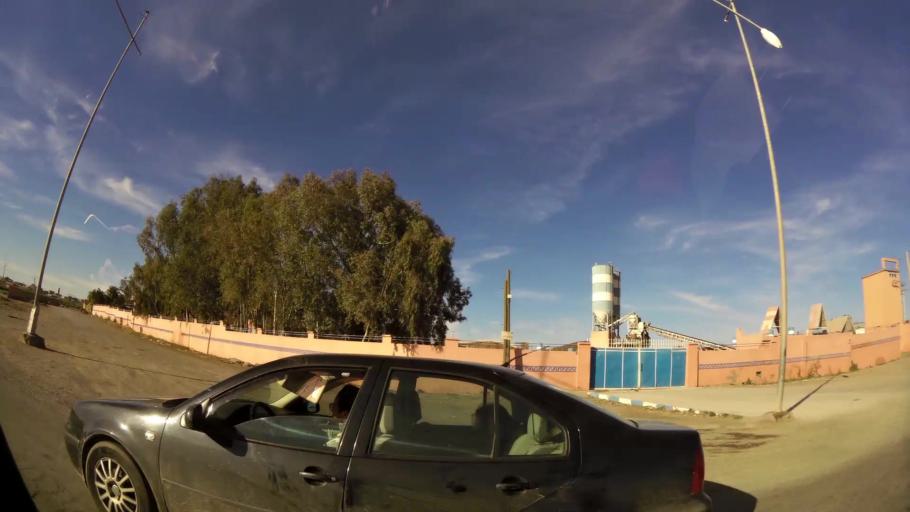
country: MA
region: Marrakech-Tensift-Al Haouz
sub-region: Marrakech
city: Marrakesh
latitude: 31.7129
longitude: -8.0722
